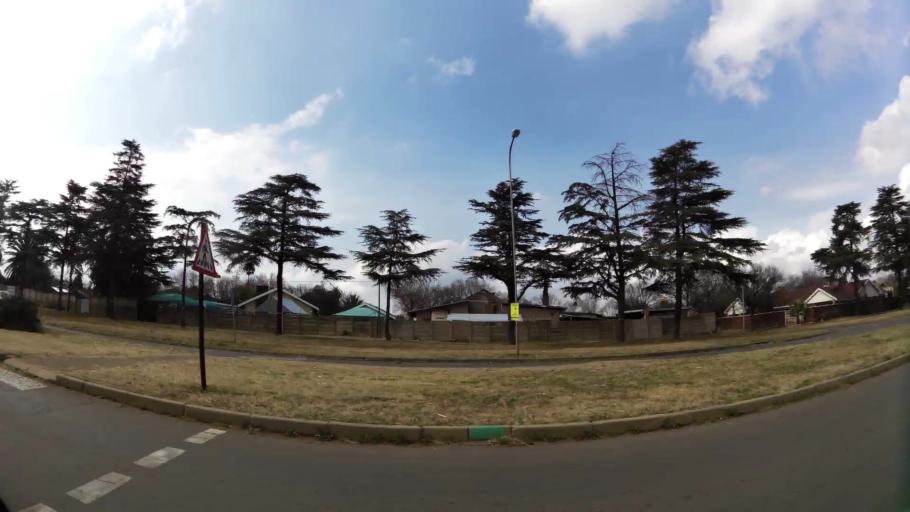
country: ZA
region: Gauteng
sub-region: Sedibeng District Municipality
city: Vanderbijlpark
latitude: -26.7159
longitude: 27.8363
